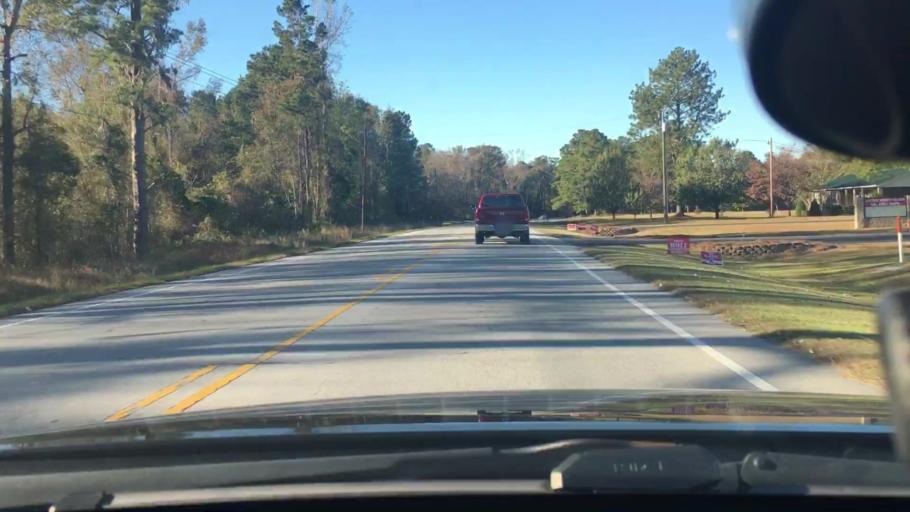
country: US
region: North Carolina
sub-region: Craven County
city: Vanceboro
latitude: 35.2271
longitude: -77.0707
